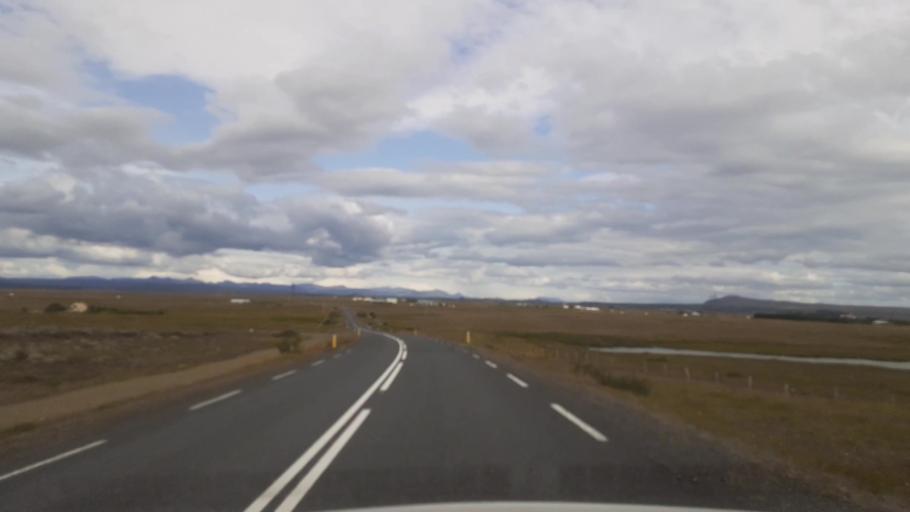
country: IS
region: South
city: Selfoss
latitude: 63.9329
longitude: -20.8424
